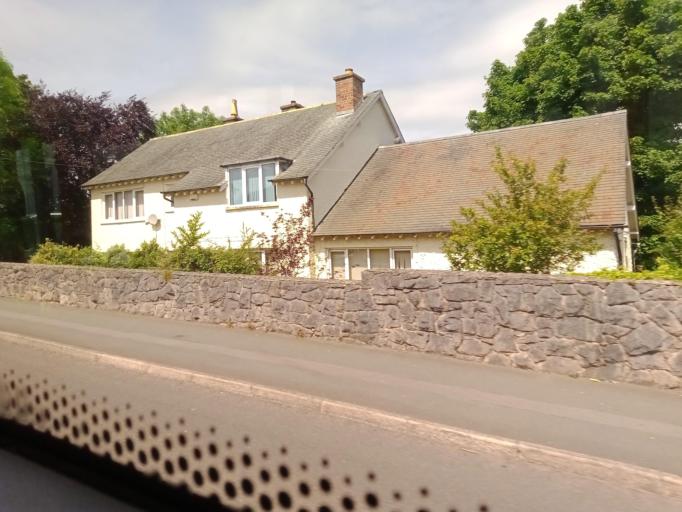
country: GB
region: Wales
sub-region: Anglesey
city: Menai Bridge
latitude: 53.2127
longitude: -4.1572
